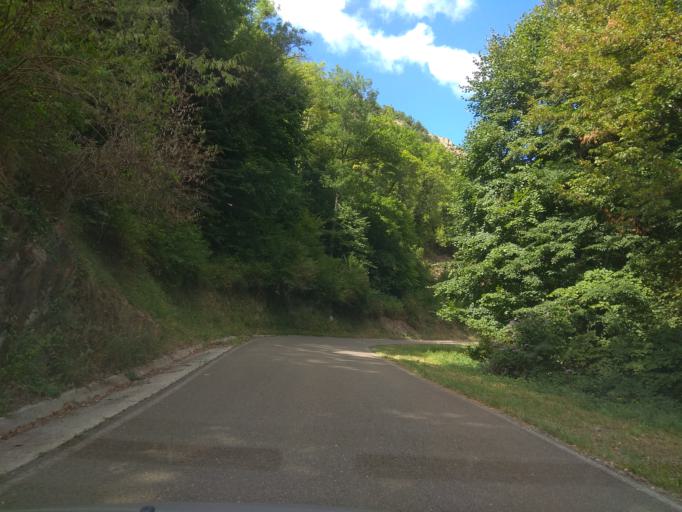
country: ES
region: Catalonia
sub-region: Provincia de Lleida
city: Les
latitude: 42.8301
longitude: 0.7252
